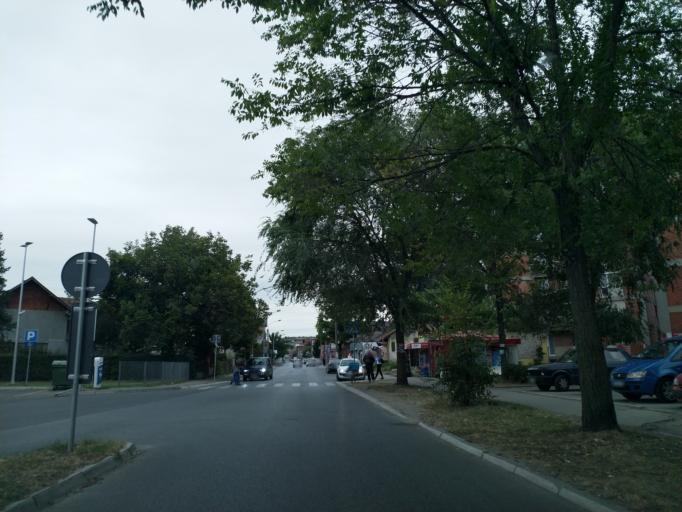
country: RS
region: Central Serbia
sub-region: Pomoravski Okrug
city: Jagodina
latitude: 43.9855
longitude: 21.2504
